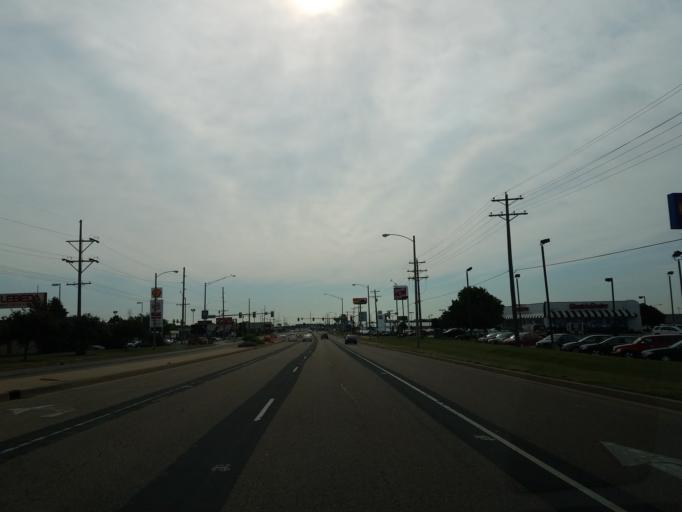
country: US
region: Illinois
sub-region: McLean County
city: Bloomington
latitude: 40.4595
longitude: -88.9772
